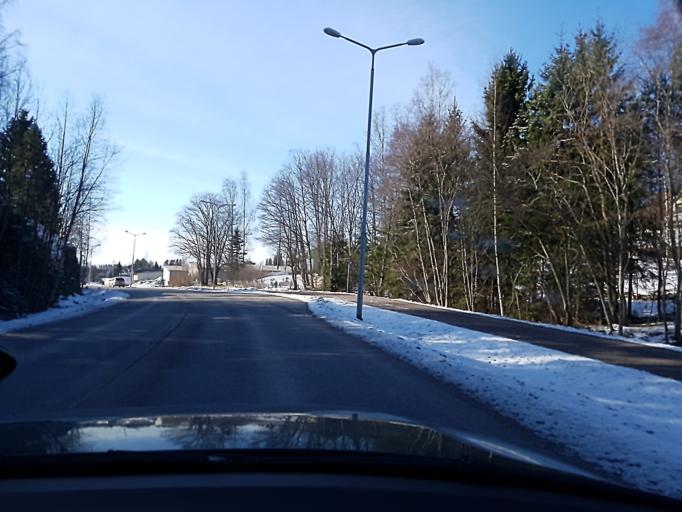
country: FI
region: Uusimaa
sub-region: Helsinki
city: Kirkkonummi
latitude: 60.1254
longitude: 24.4279
